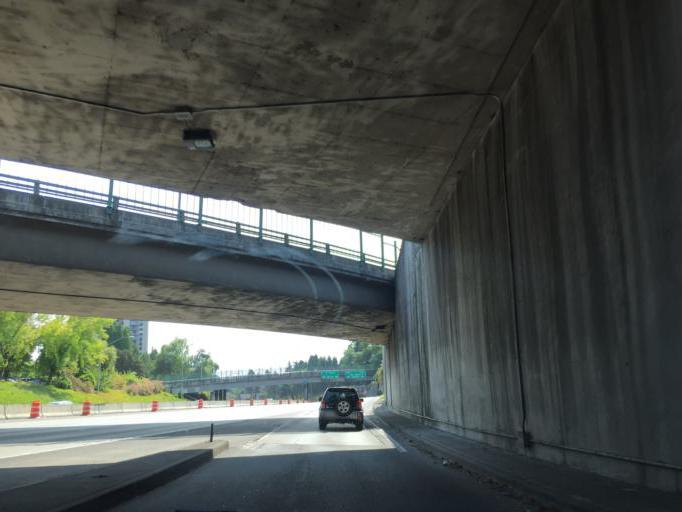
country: US
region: Oregon
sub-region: Multnomah County
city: Portland
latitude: 45.5075
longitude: -122.6842
